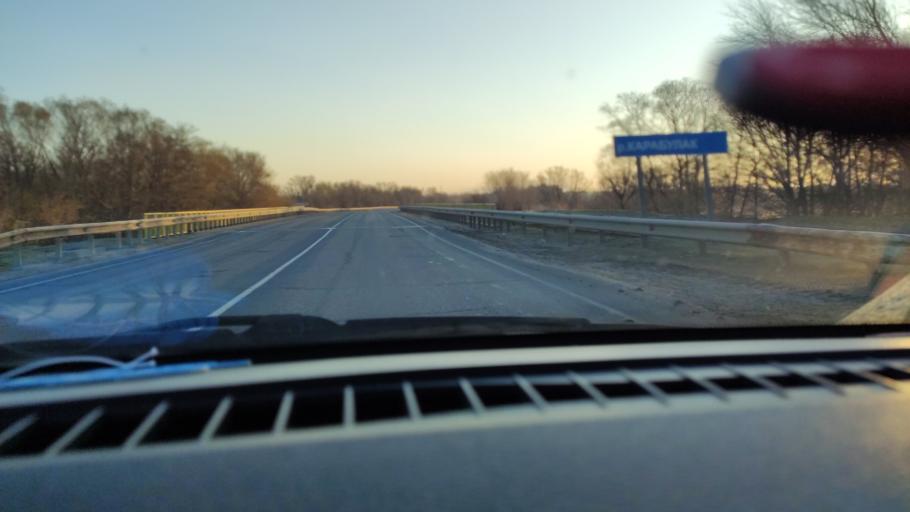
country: RU
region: Saratov
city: Sinodskoye
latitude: 51.9761
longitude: 46.6477
